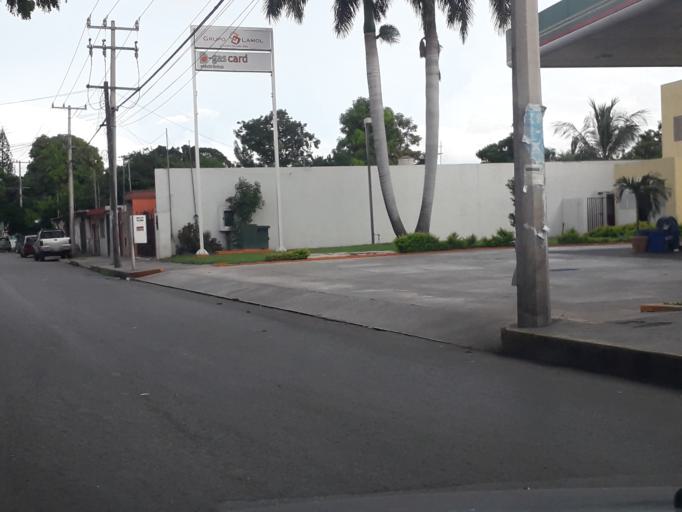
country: MX
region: Yucatan
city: Merida
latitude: 20.9614
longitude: -89.6633
